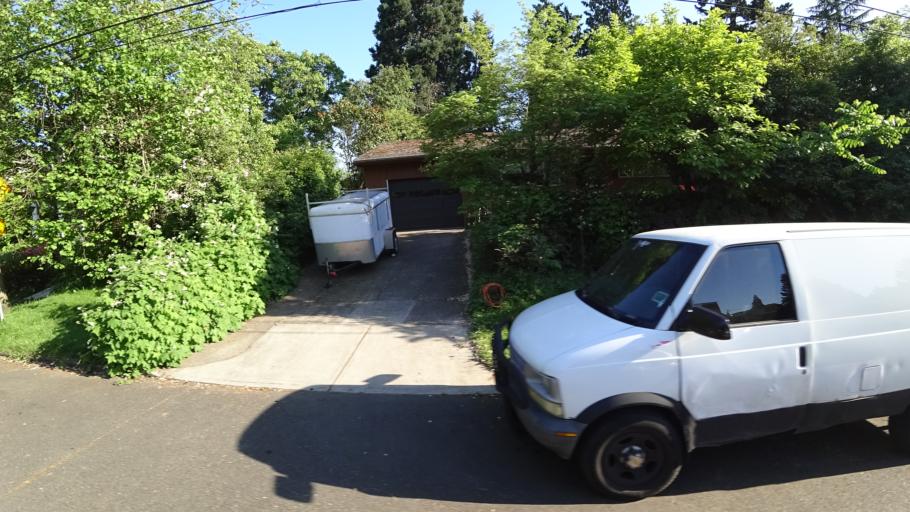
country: US
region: Oregon
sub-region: Multnomah County
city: Portland
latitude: 45.5590
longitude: -122.6914
